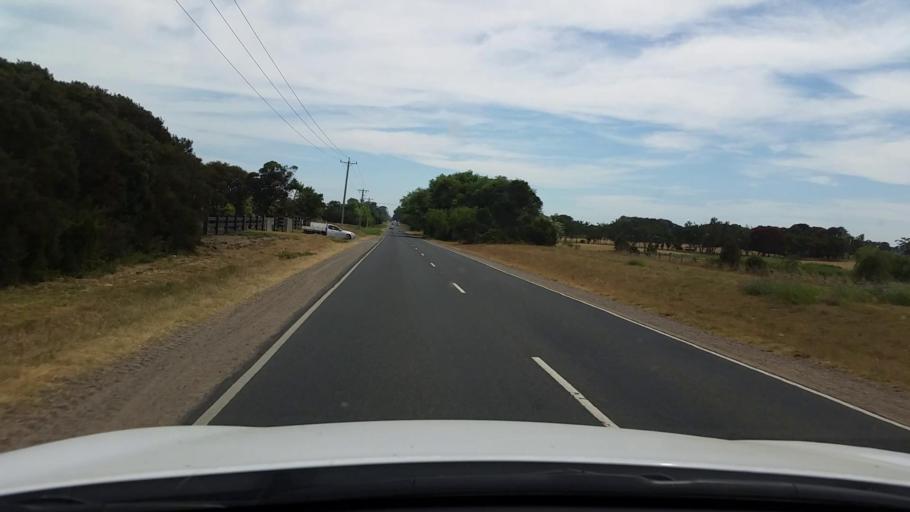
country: AU
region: Victoria
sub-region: Mornington Peninsula
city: Rosebud West
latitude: -38.4066
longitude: 144.8877
